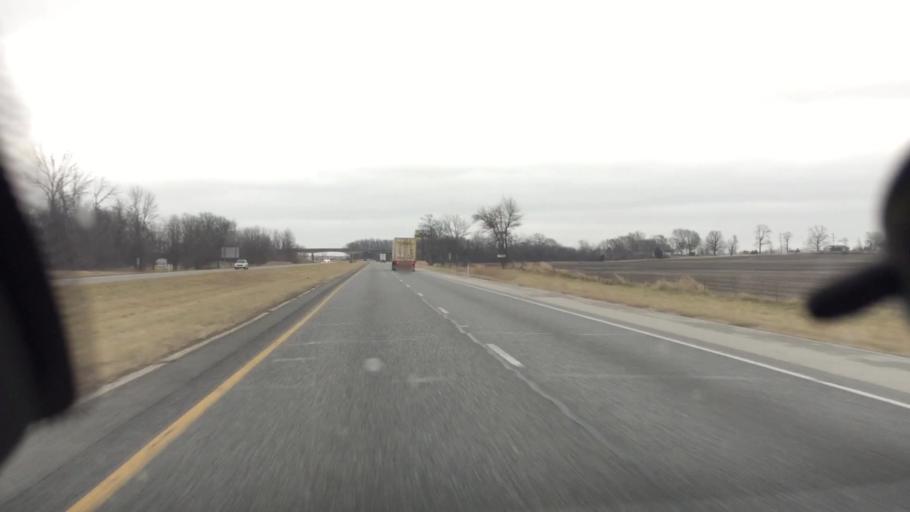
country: US
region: Indiana
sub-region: Hendricks County
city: Pittsboro
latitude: 39.8835
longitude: -86.5155
